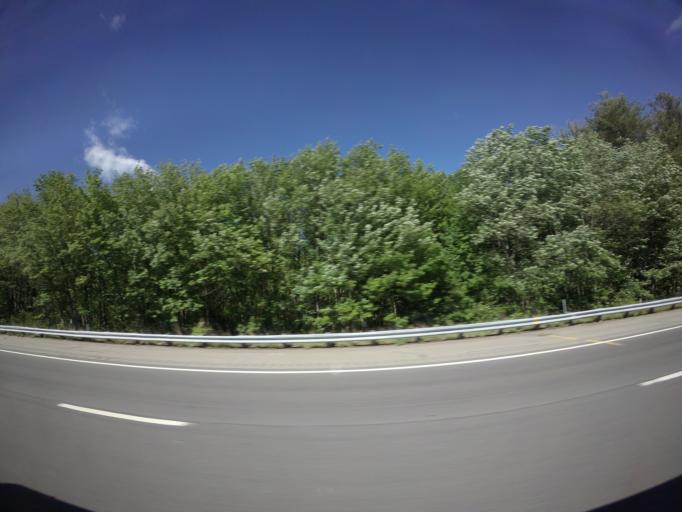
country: US
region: New Hampshire
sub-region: Hillsborough County
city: Manchester
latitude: 42.9517
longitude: -71.3995
